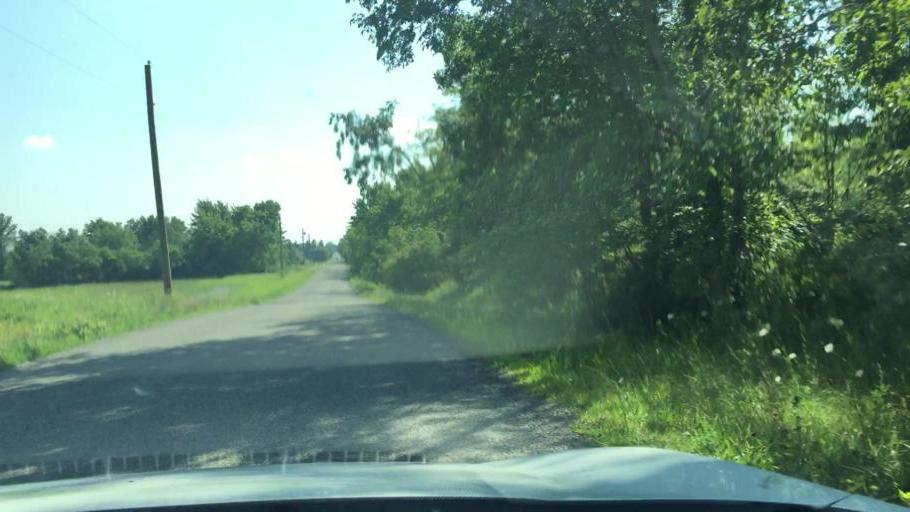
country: US
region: Ohio
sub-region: Champaign County
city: North Lewisburg
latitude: 40.2634
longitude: -83.5035
